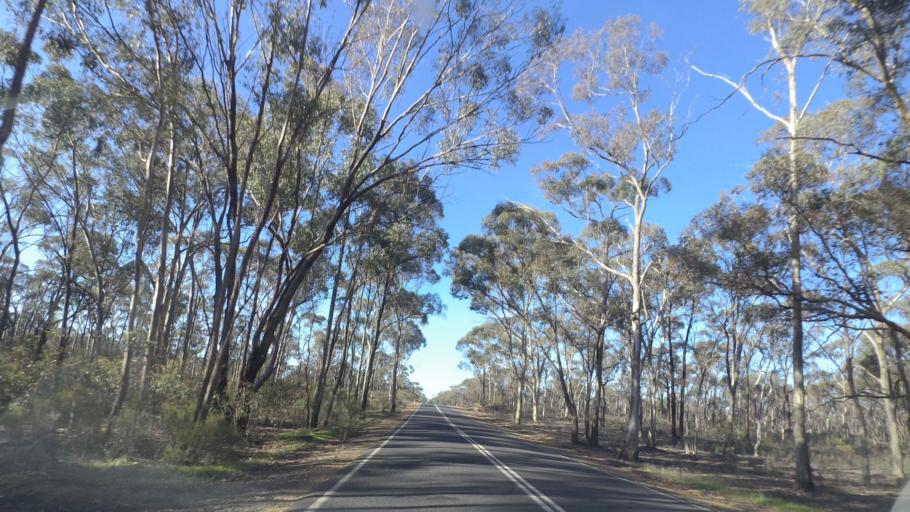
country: AU
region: Victoria
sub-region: Greater Bendigo
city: Epsom
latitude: -36.6670
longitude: 144.4326
